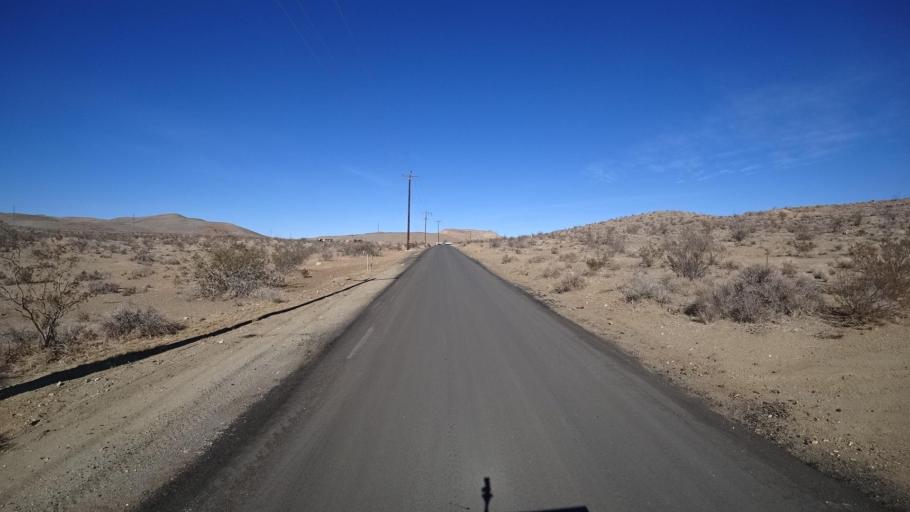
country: US
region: California
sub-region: Kern County
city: Ridgecrest
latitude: 35.3411
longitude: -117.6319
